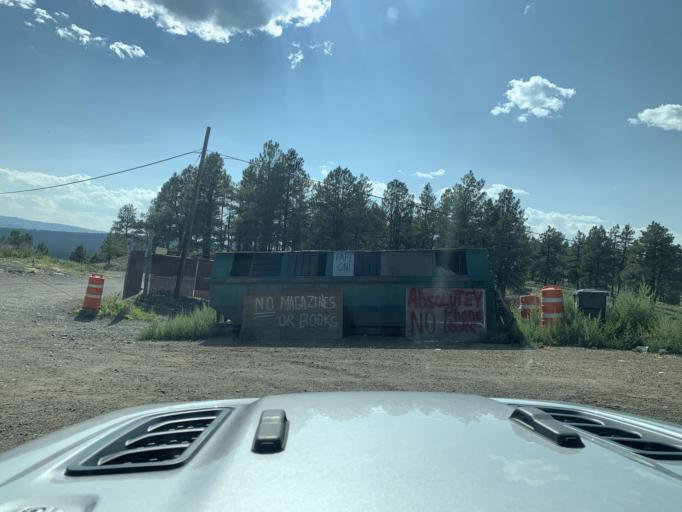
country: US
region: Colorado
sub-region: Archuleta County
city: Pagosa Springs
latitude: 37.2406
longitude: -107.0248
